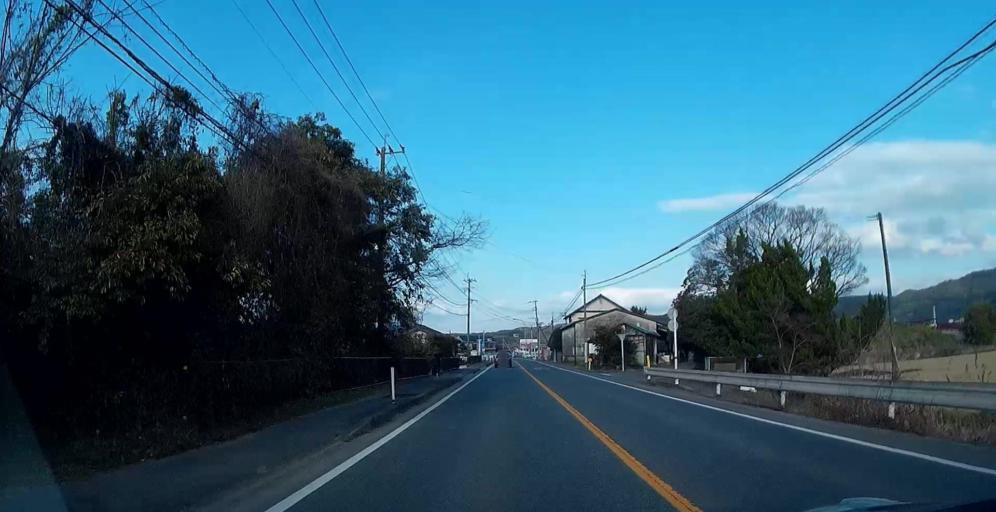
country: JP
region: Kumamoto
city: Matsubase
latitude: 32.6075
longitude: 130.7046
